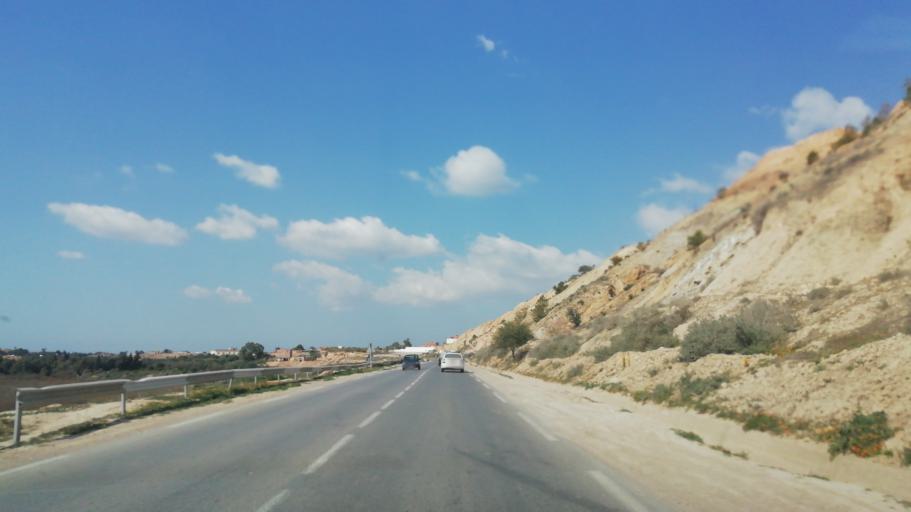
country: DZ
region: Mascara
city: Mascara
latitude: 35.5675
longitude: 0.0713
